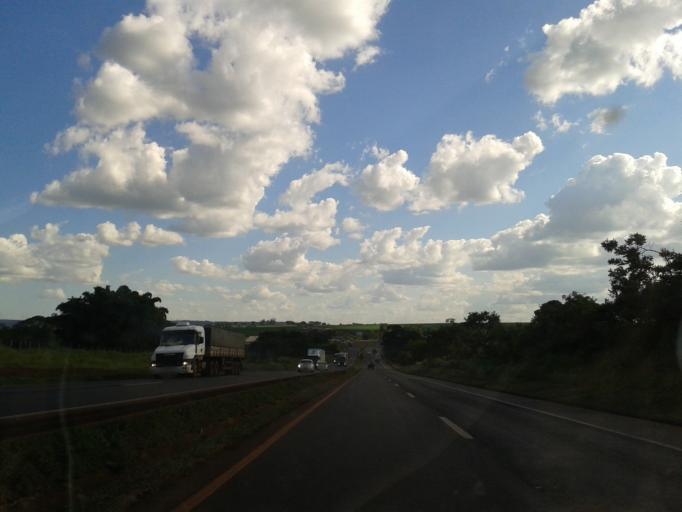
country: BR
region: Minas Gerais
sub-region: Centralina
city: Centralina
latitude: -18.5356
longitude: -49.1927
